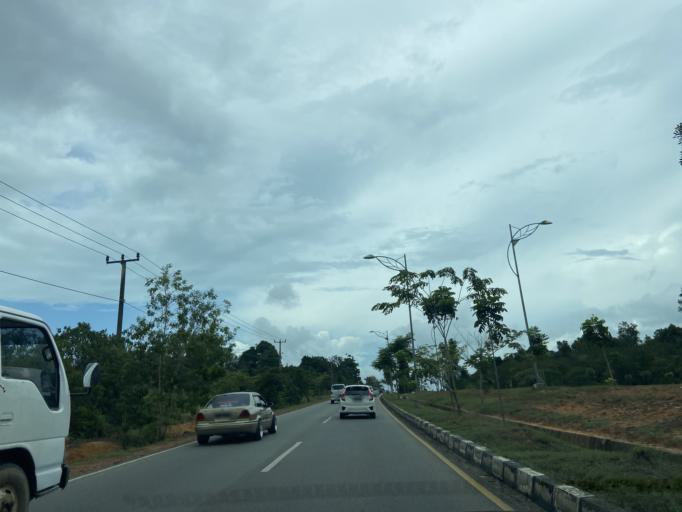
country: SG
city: Singapore
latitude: 1.1313
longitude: 104.1100
